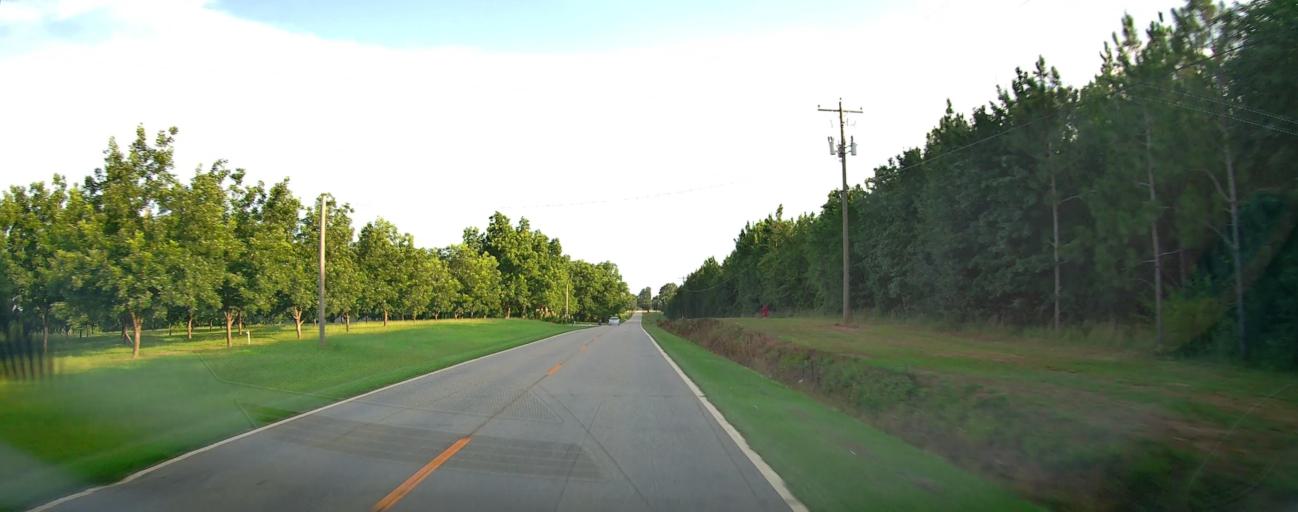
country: US
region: Georgia
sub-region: Peach County
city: Byron
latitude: 32.6685
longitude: -83.8609
